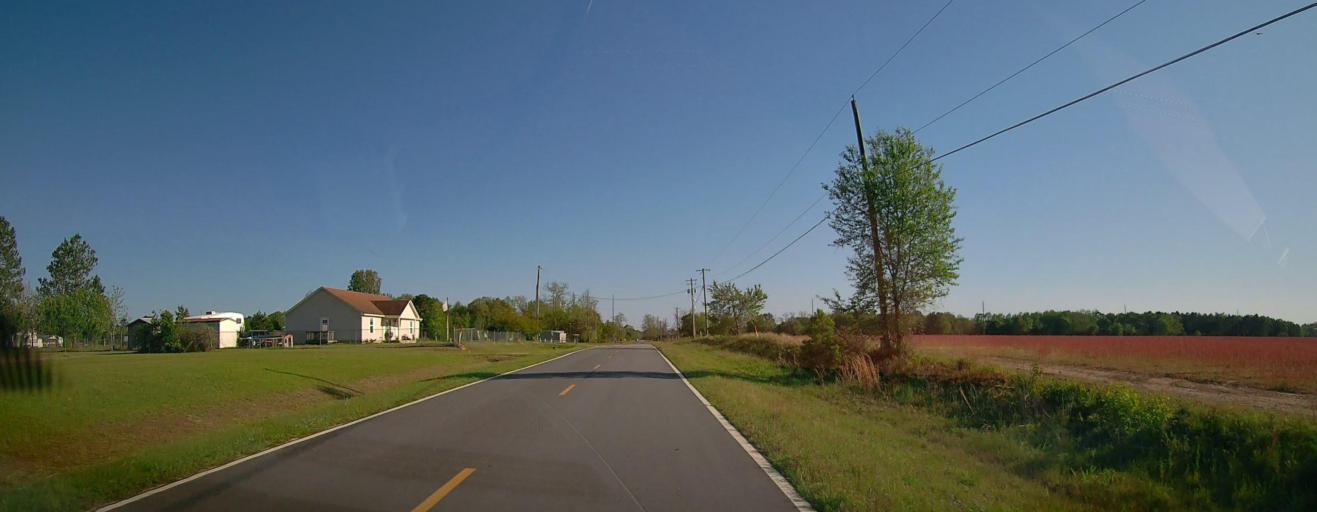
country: US
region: Georgia
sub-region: Ben Hill County
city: Fitzgerald
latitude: 31.7384
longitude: -83.2802
